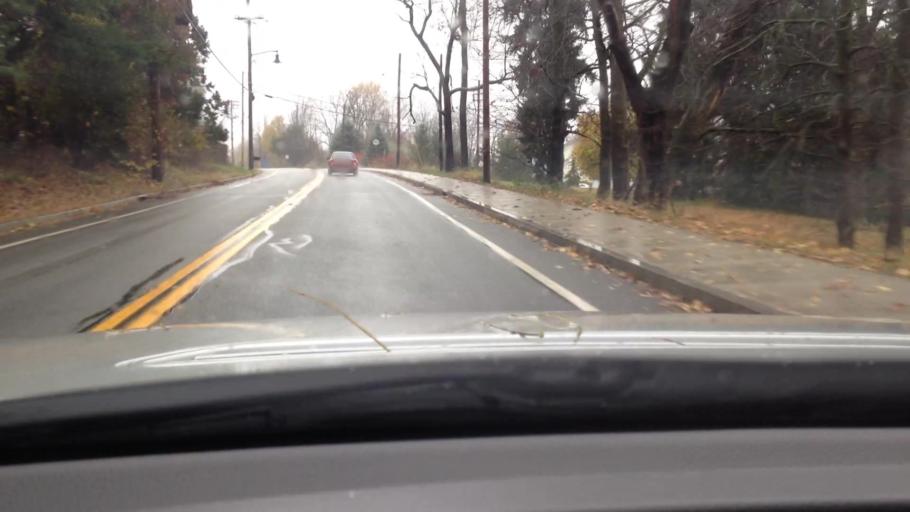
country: US
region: New York
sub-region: Dutchess County
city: Beacon
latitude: 41.4862
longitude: -73.9679
